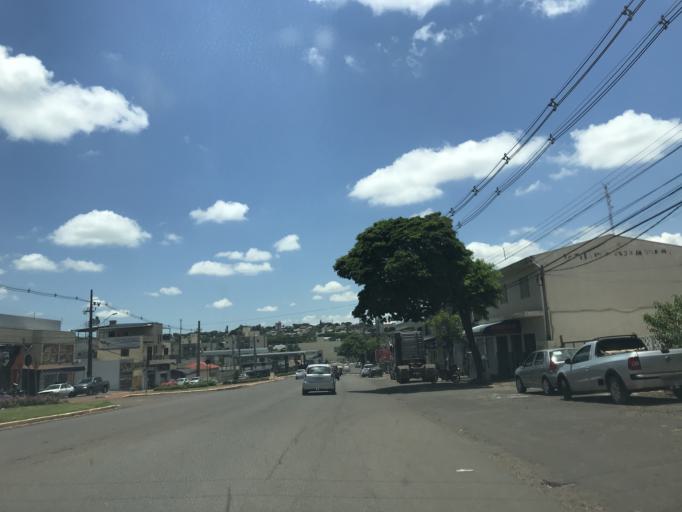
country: BR
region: Parana
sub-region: Marialva
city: Marialva
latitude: -23.4792
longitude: -51.8053
